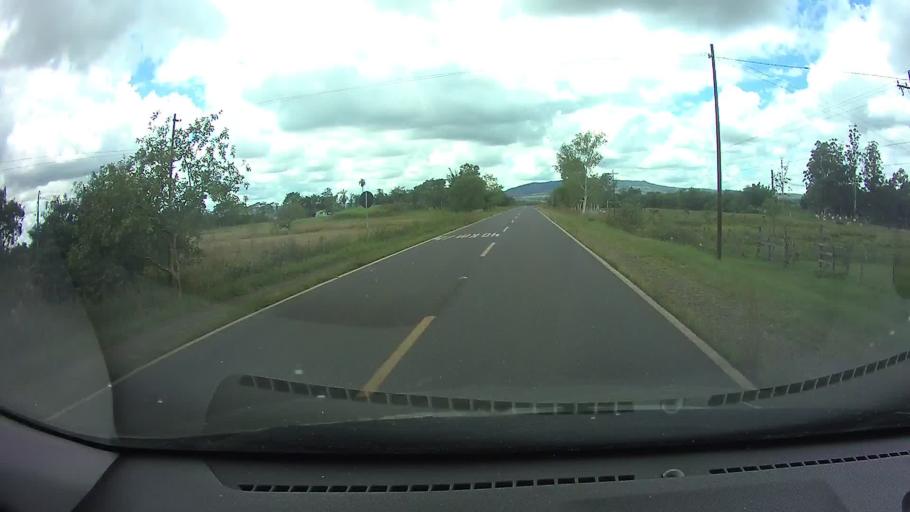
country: PY
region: Paraguari
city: Ybycui
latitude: -25.9133
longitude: -57.0360
